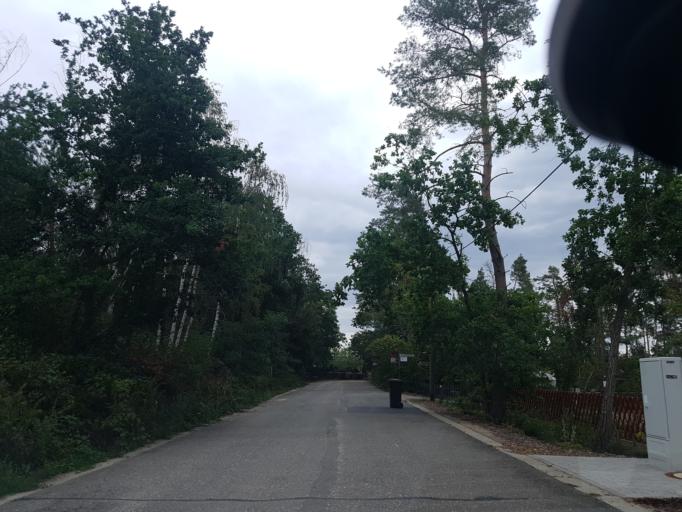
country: DE
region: Brandenburg
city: Bad Liebenwerda
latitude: 51.5045
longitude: 13.4372
